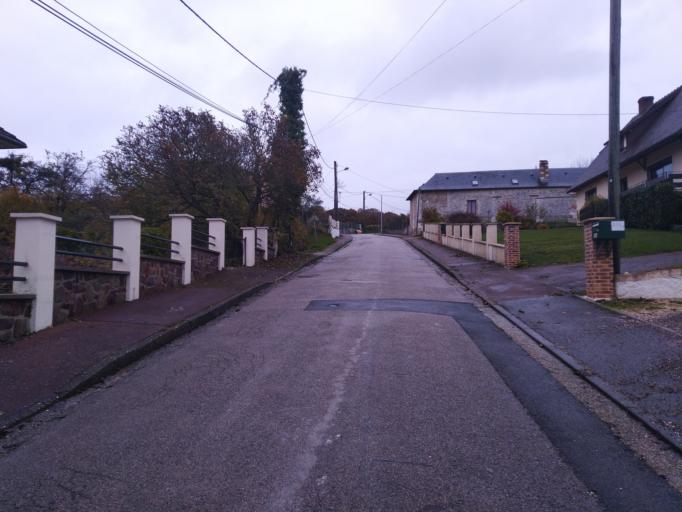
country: FR
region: Haute-Normandie
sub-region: Departement de la Seine-Maritime
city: Yainville
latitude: 49.4559
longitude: 0.8358
